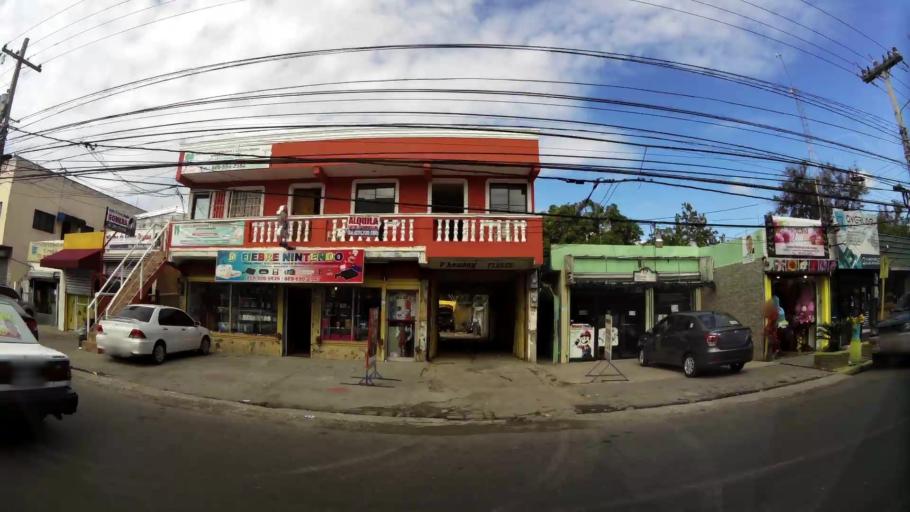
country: DO
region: Santo Domingo
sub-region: Santo Domingo
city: Santo Domingo Este
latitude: 18.4931
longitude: -69.8652
